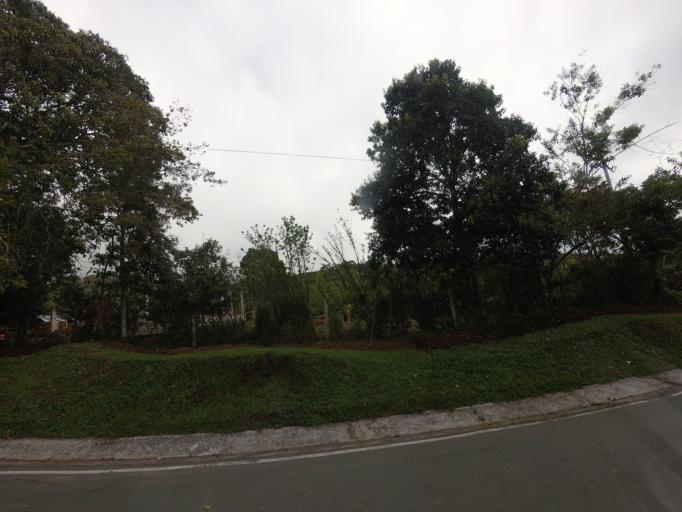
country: CO
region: Huila
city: San Agustin
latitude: 1.8874
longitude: -76.2843
